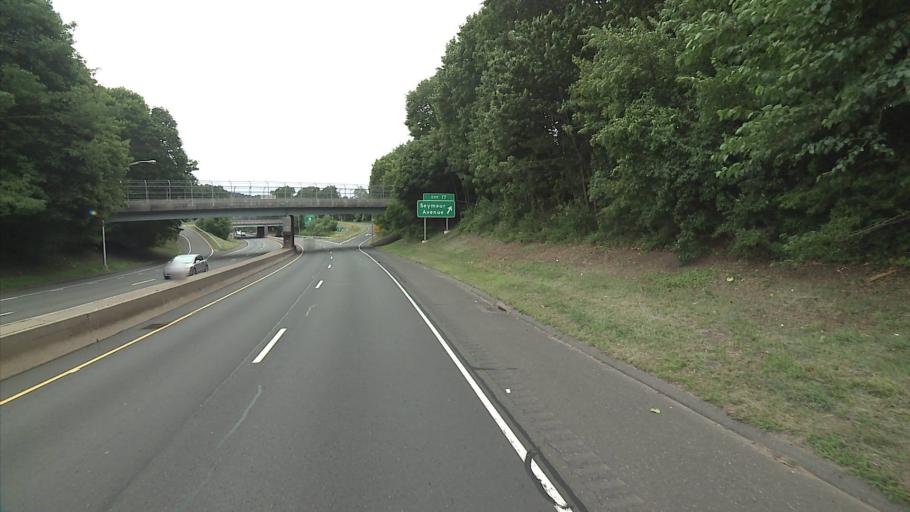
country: US
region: Connecticut
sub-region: New Haven County
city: Derby
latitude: 41.3316
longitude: -73.0912
